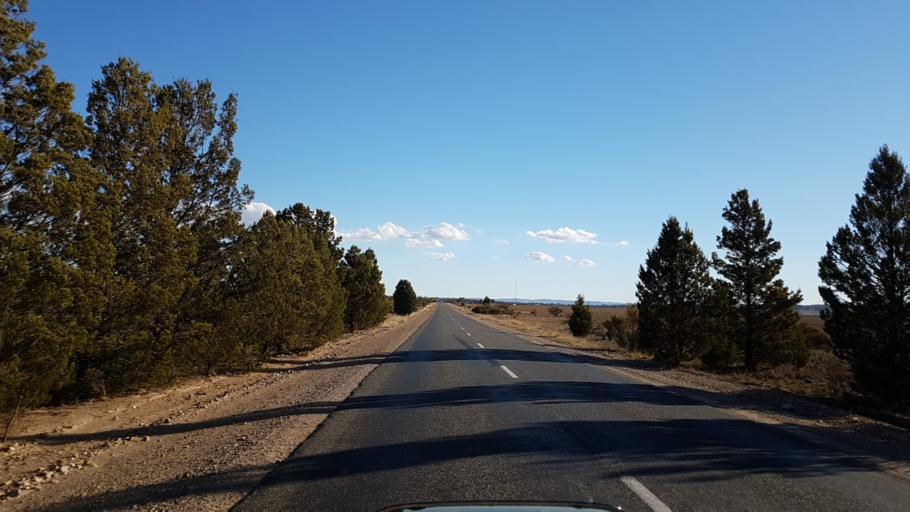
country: AU
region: South Australia
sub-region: Peterborough
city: Peterborough
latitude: -32.9627
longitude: 138.8851
